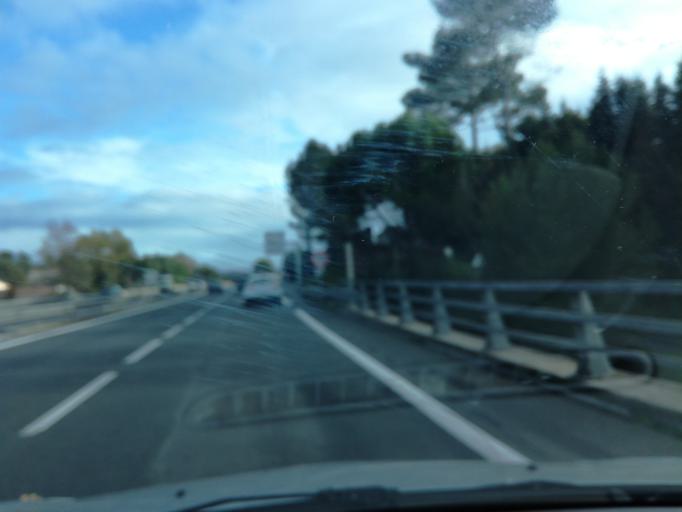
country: FR
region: Provence-Alpes-Cote d'Azur
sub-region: Departement des Alpes-Maritimes
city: Mouans-Sartoux
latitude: 43.6140
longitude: 6.9629
